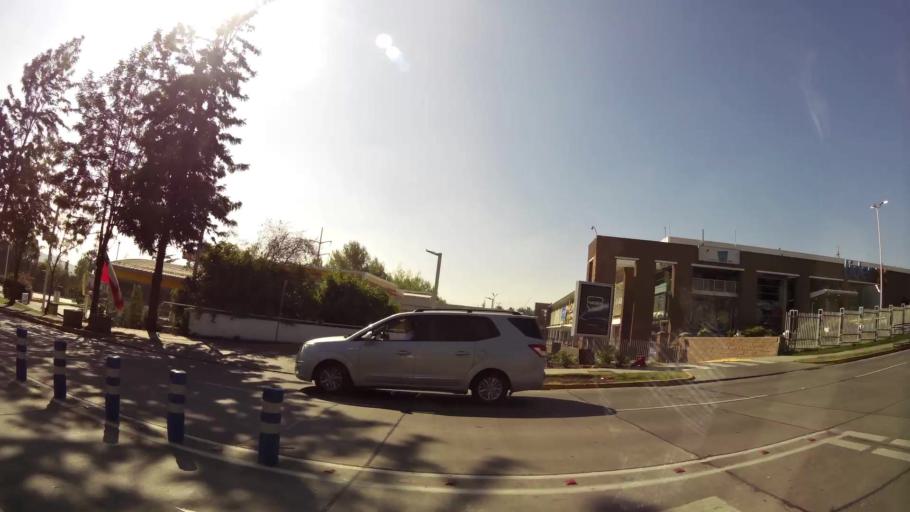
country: CL
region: Santiago Metropolitan
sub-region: Provincia de Santiago
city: Villa Presidente Frei, Nunoa, Santiago, Chile
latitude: -33.4029
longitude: -70.5163
